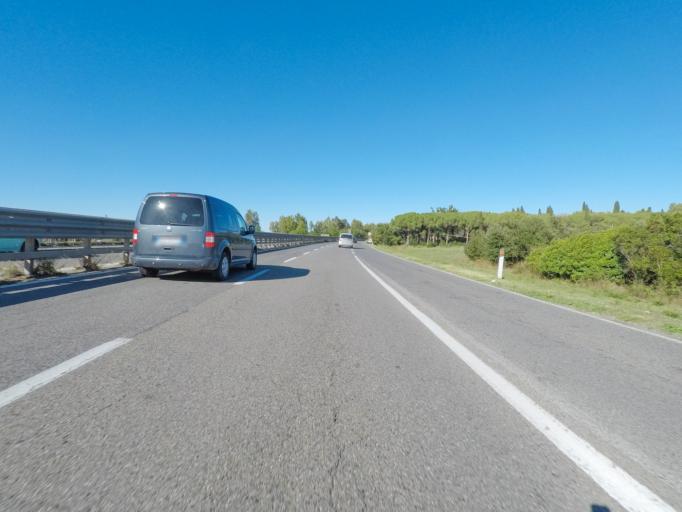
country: IT
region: Tuscany
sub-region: Provincia di Grosseto
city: Grosseto
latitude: 42.7025
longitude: 11.1374
